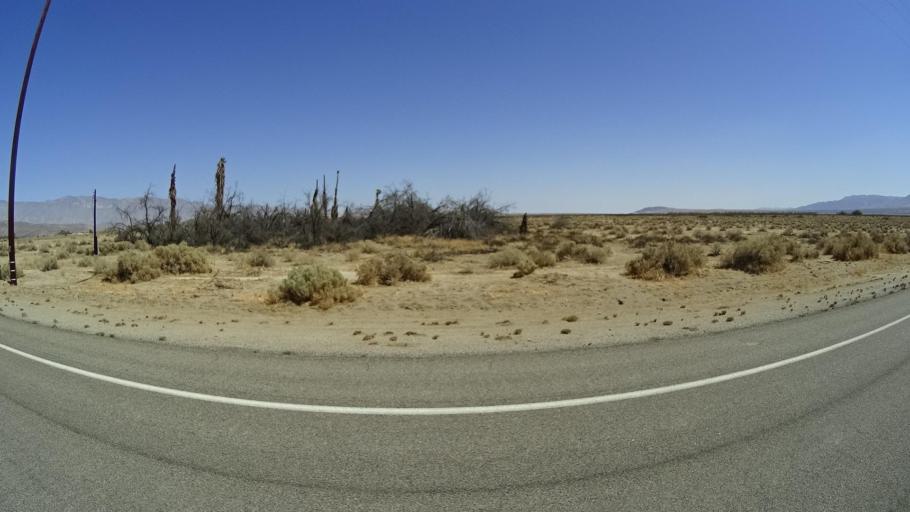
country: US
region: California
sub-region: San Diego County
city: Borrego Springs
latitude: 33.2526
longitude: -116.3479
